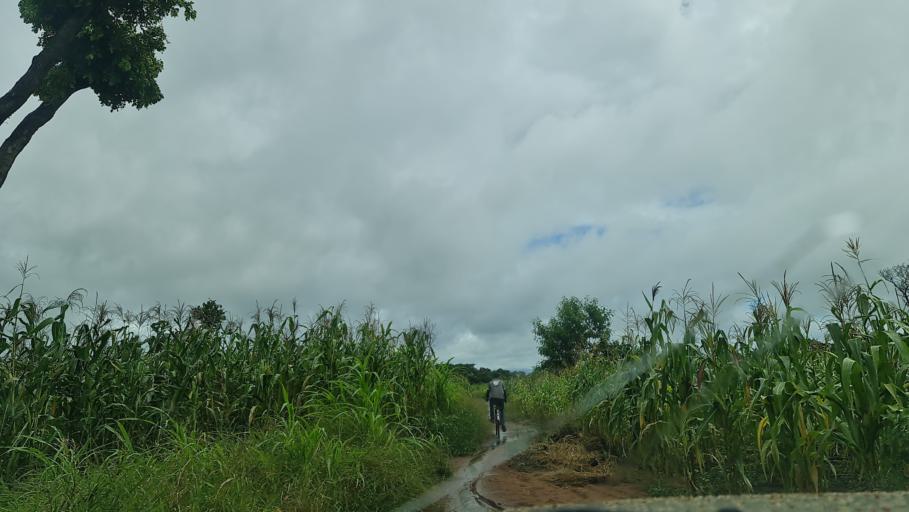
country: MW
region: Southern Region
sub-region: Nsanje District
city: Nsanje
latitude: -17.4440
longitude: 35.8453
